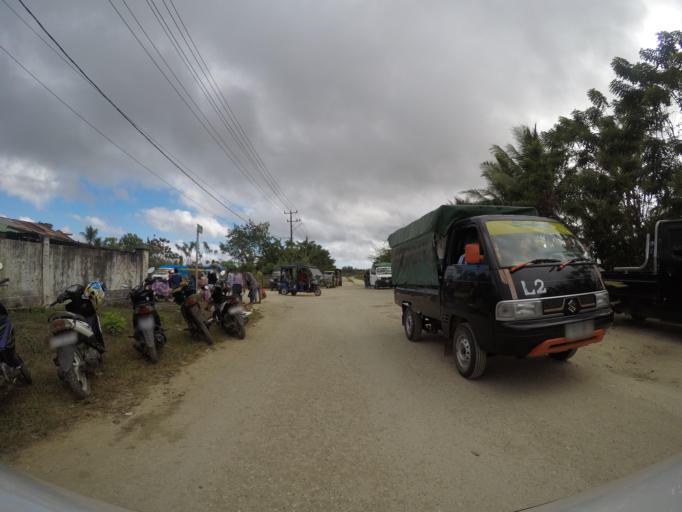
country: TL
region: Lautem
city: Lospalos
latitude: -8.5120
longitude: 127.0049
